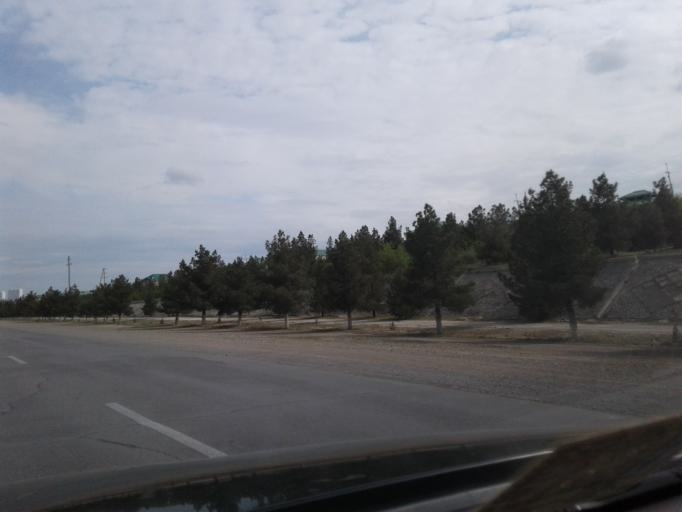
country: TM
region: Ahal
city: Ashgabat
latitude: 37.9609
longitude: 58.3150
